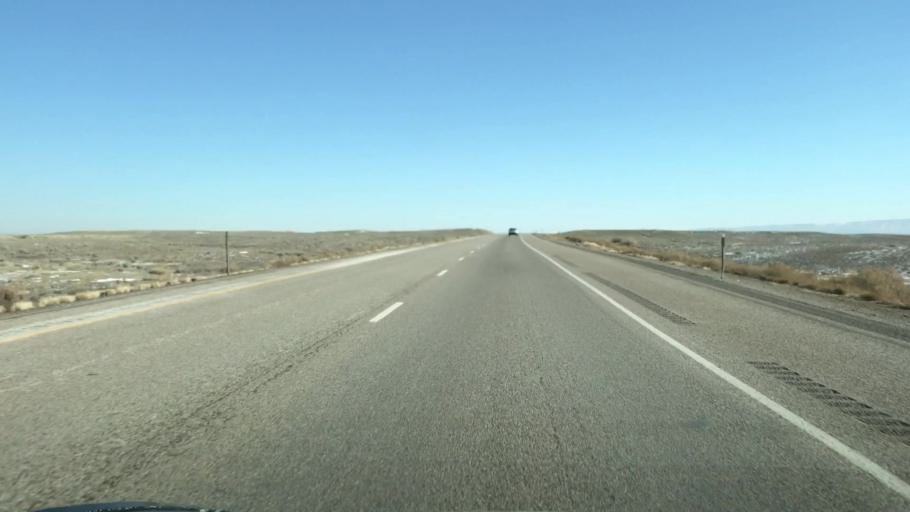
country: US
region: Utah
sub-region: Grand County
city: Moab
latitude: 38.9674
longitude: -109.3676
